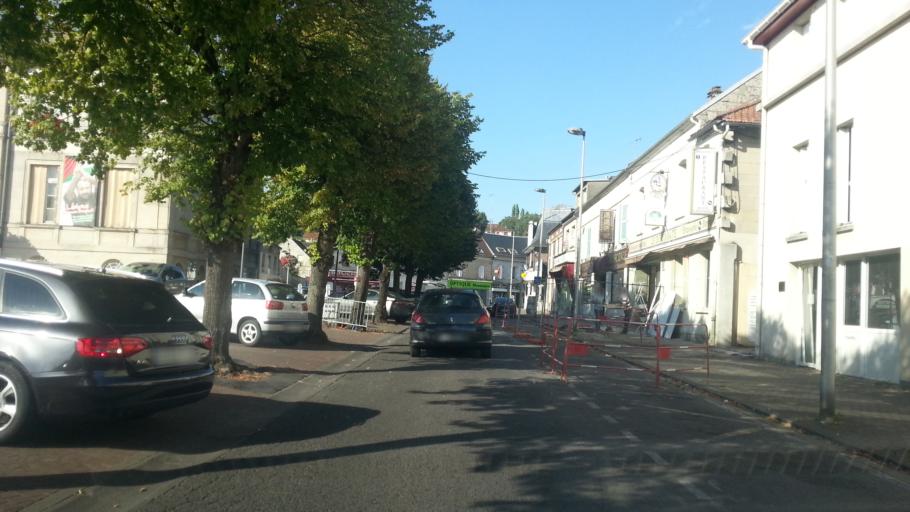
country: FR
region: Picardie
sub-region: Departement de l'Oise
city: Thiverny
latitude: 49.2559
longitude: 2.4346
